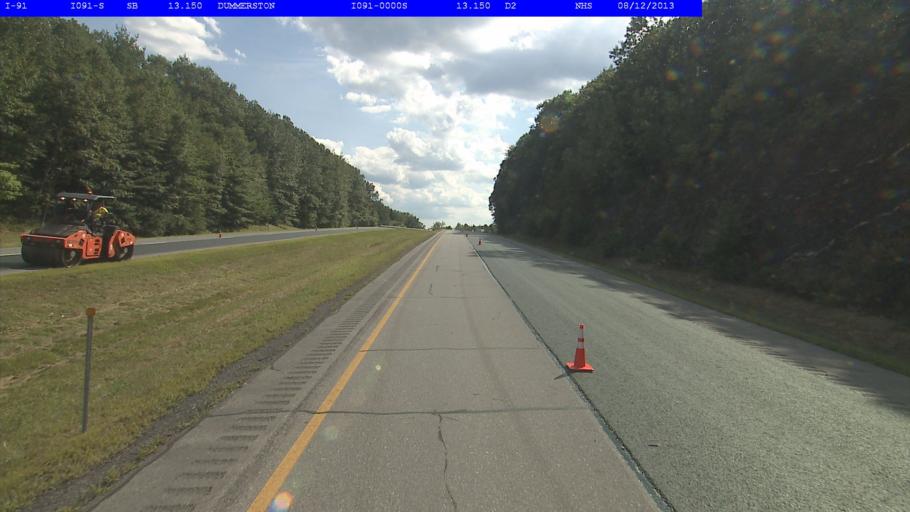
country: US
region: Vermont
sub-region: Windham County
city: Brattleboro
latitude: 42.9012
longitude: -72.5376
